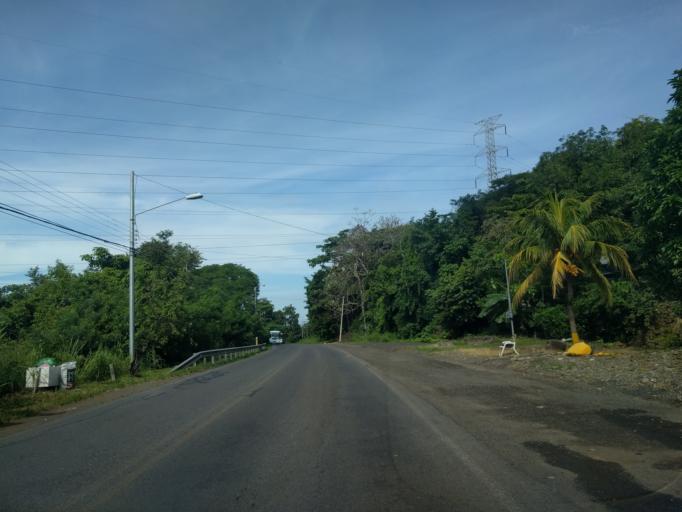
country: CR
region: Puntarenas
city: Esparza
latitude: 9.9917
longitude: -84.7062
